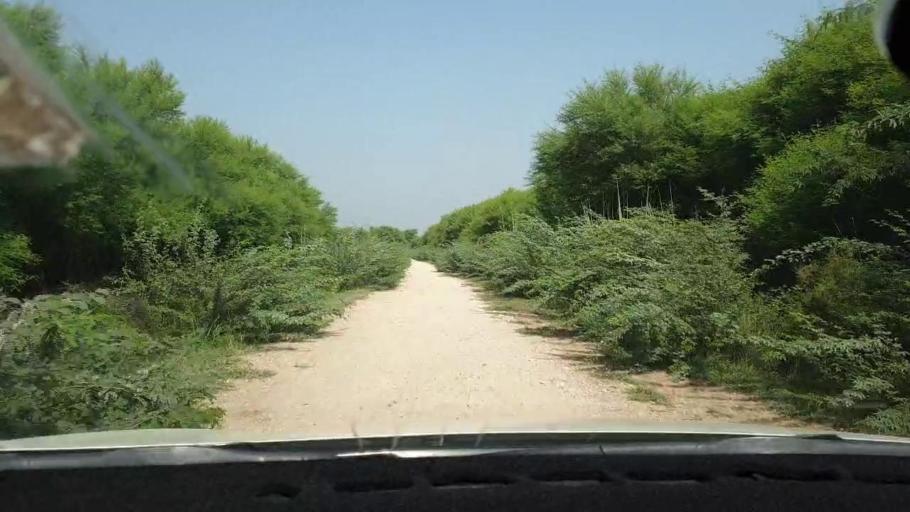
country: PK
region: Sindh
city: Tando Mittha Khan
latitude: 25.9457
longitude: 69.2982
